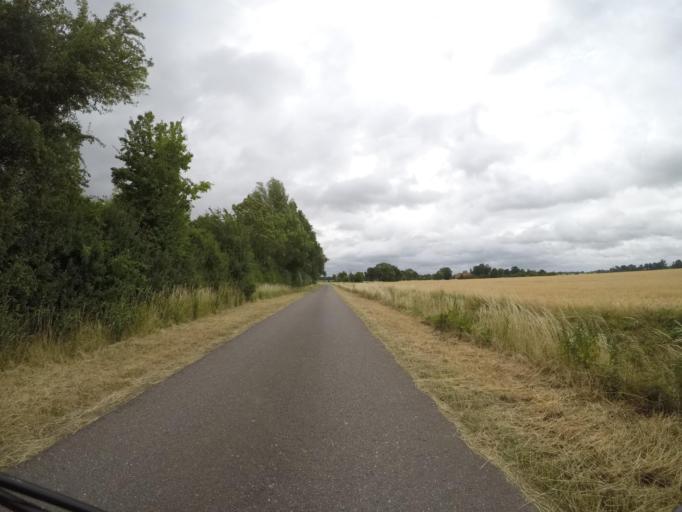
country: DE
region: Lower Saxony
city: Hitzacker
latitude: 53.1635
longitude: 11.1084
